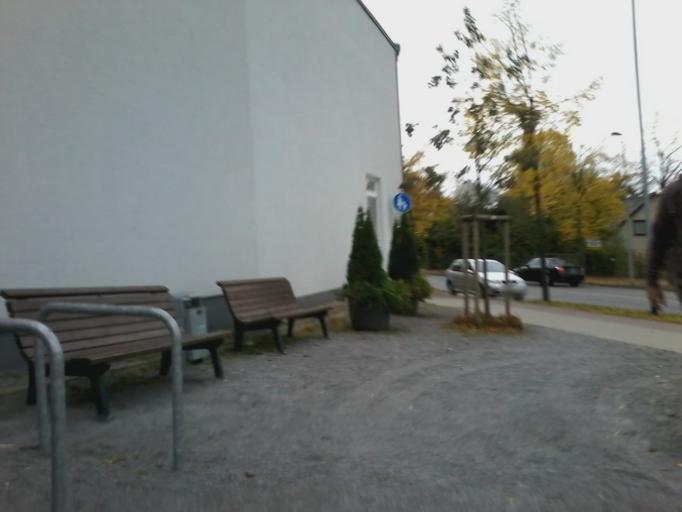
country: DE
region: Lower Saxony
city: Achim
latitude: 53.0129
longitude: 9.0333
